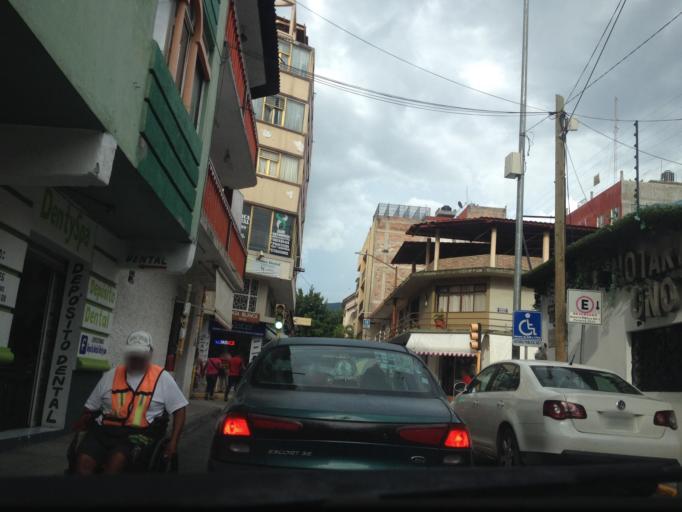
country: MX
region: Guerrero
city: Chilpancingo de los Bravos
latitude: 17.5527
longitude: -99.5029
